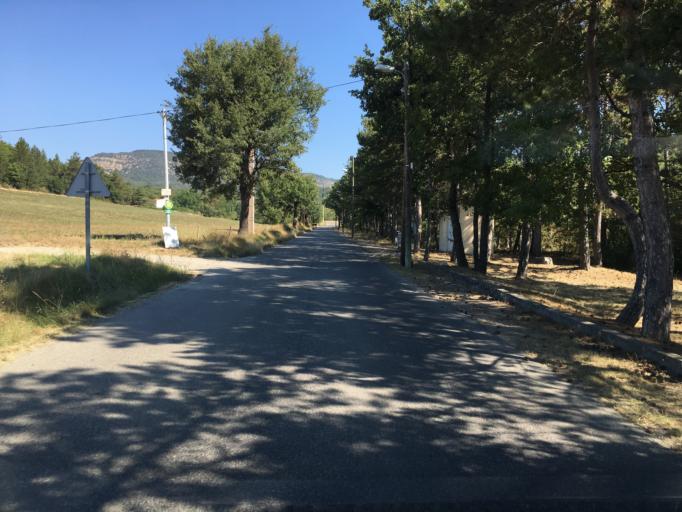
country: FR
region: Provence-Alpes-Cote d'Azur
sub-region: Departement des Alpes-de-Haute-Provence
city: Mallemoisson
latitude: 44.0526
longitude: 6.1485
